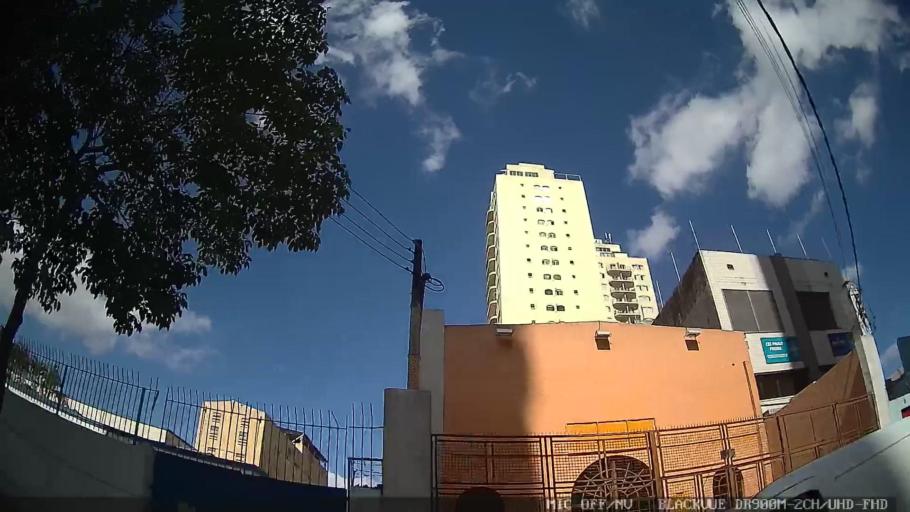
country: BR
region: Sao Paulo
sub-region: Sao Caetano Do Sul
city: Sao Caetano do Sul
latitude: -23.6129
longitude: -46.5973
